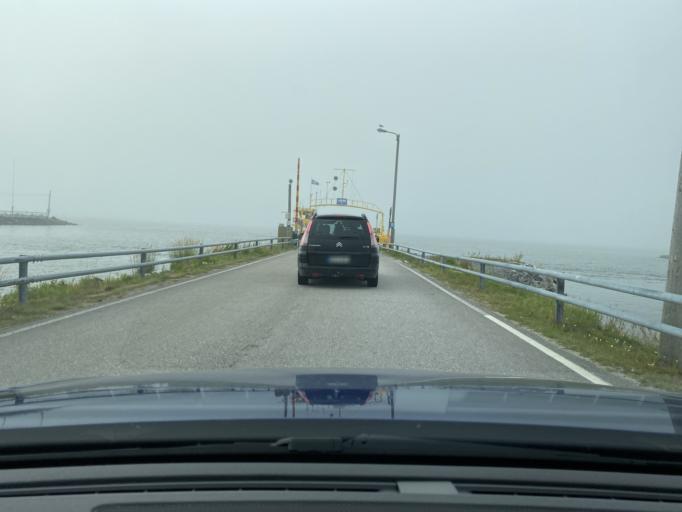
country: FI
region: Ostrobothnia
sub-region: Vaasa
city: Korsnaes
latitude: 62.9341
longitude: 21.1872
